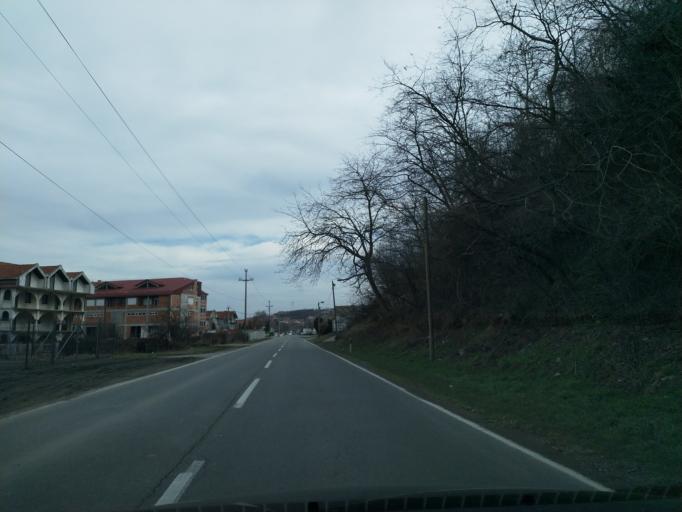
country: RS
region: Central Serbia
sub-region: Belgrade
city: Zvezdara
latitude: 44.7279
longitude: 20.5674
